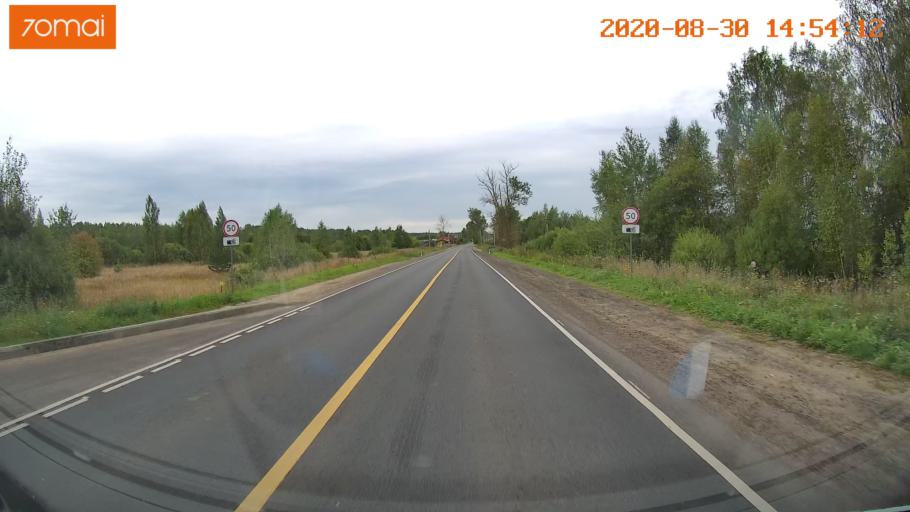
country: RU
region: Ivanovo
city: Kineshma
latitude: 57.3956
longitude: 42.0467
